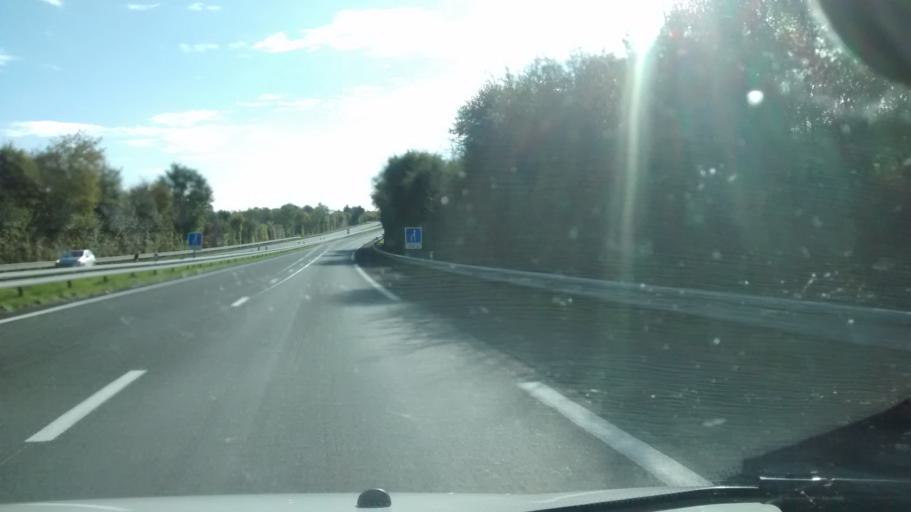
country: FR
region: Pays de la Loire
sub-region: Departement de Maine-et-Loire
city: Pouance
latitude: 47.7521
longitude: -1.1606
